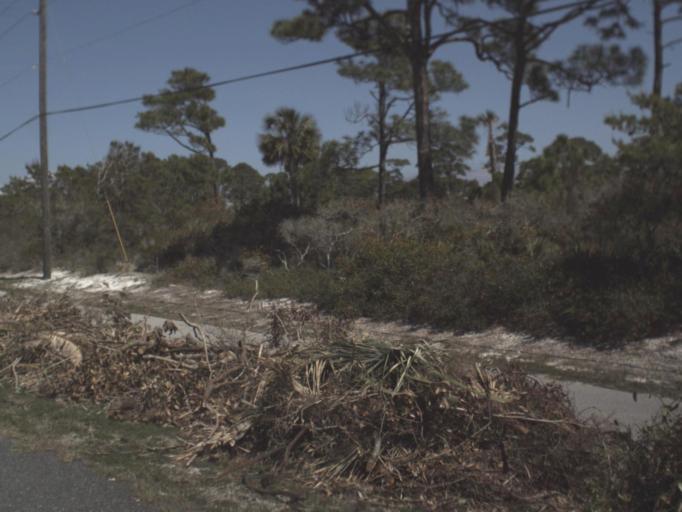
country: US
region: Florida
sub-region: Gulf County
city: Port Saint Joe
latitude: 29.7429
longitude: -85.3955
